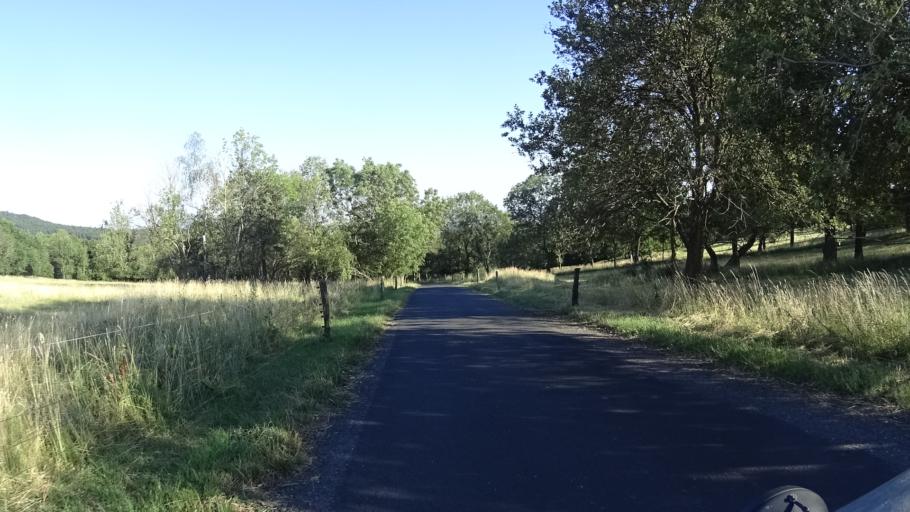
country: CZ
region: Ustecky
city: Zitenice
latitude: 50.5880
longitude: 14.1233
